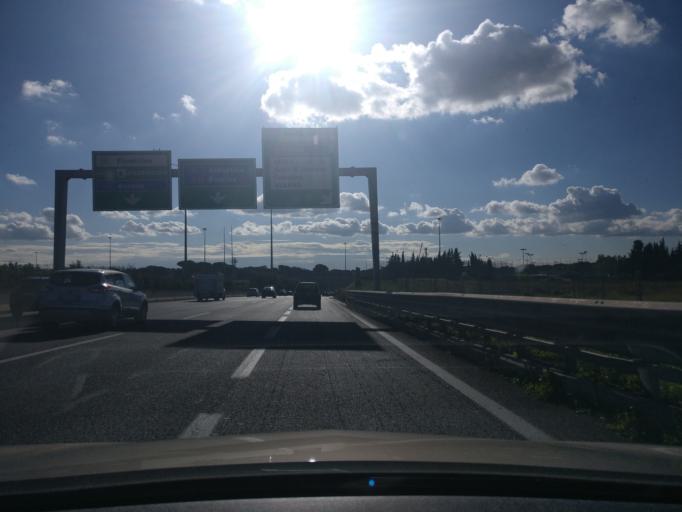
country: IT
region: Latium
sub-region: Citta metropolitana di Roma Capitale
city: Ciampino
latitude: 41.8161
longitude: 12.5759
